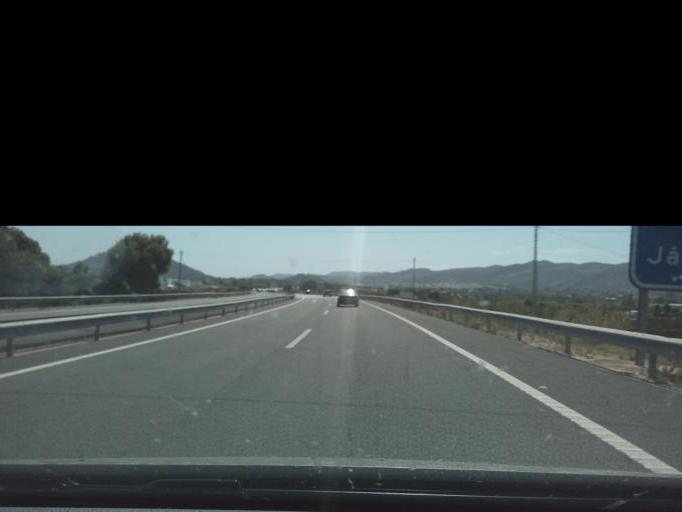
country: ES
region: Valencia
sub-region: Provincia de Alicante
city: Ondara
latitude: 38.8212
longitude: 0.0106
